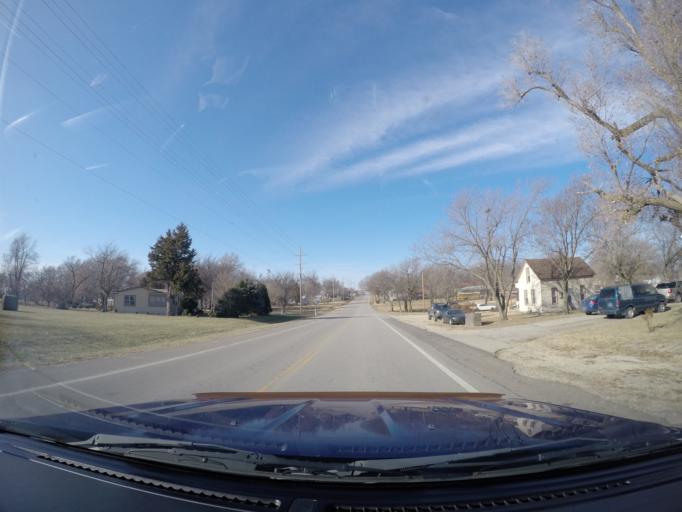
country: US
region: Kansas
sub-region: Riley County
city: Fort Riley North
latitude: 39.3644
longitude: -96.8529
